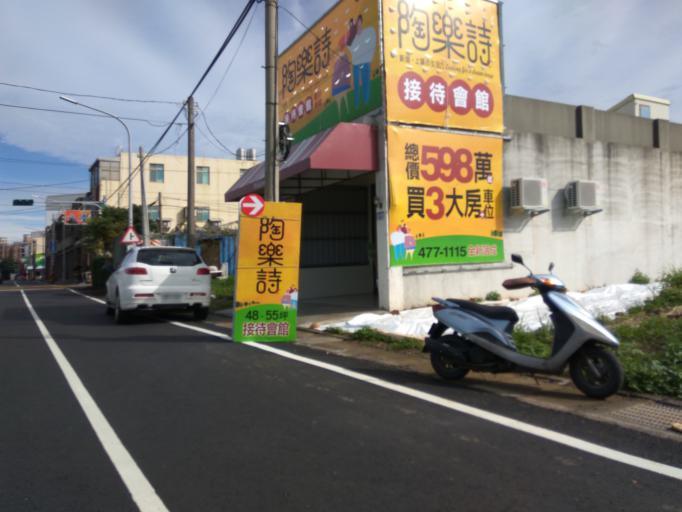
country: TW
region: Taiwan
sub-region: Hsinchu
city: Zhubei
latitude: 24.9791
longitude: 121.1070
